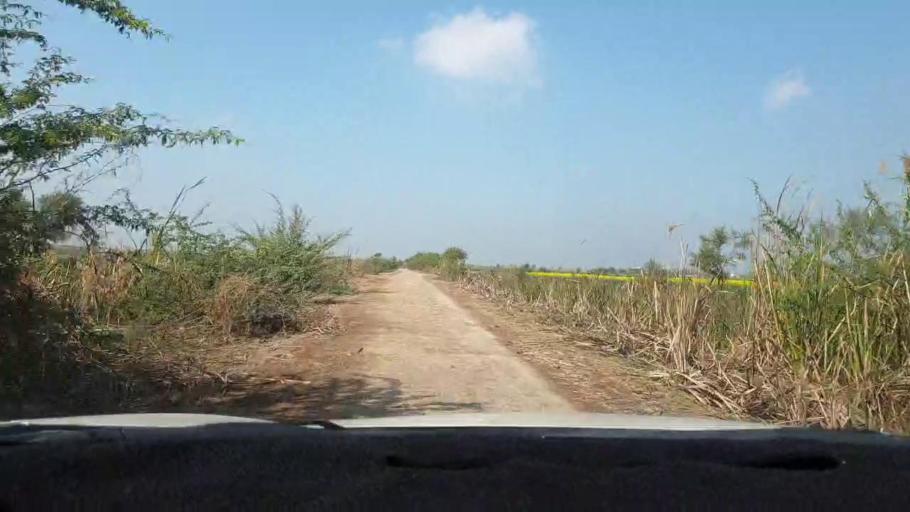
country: PK
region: Sindh
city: Berani
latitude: 25.7672
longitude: 68.8621
